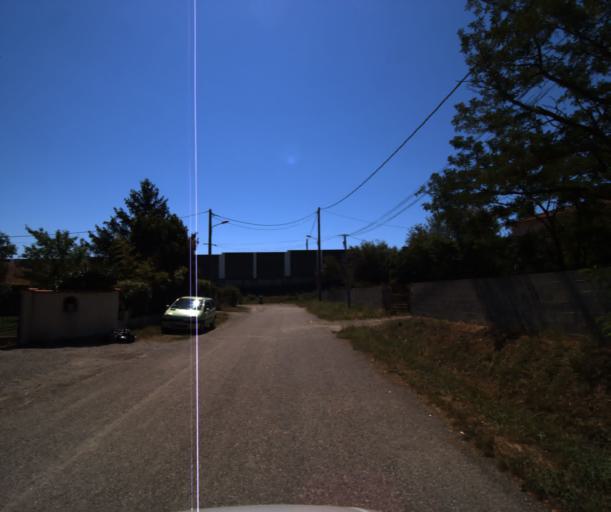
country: FR
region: Midi-Pyrenees
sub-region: Departement de la Haute-Garonne
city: Seysses
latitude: 43.4671
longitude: 1.3136
